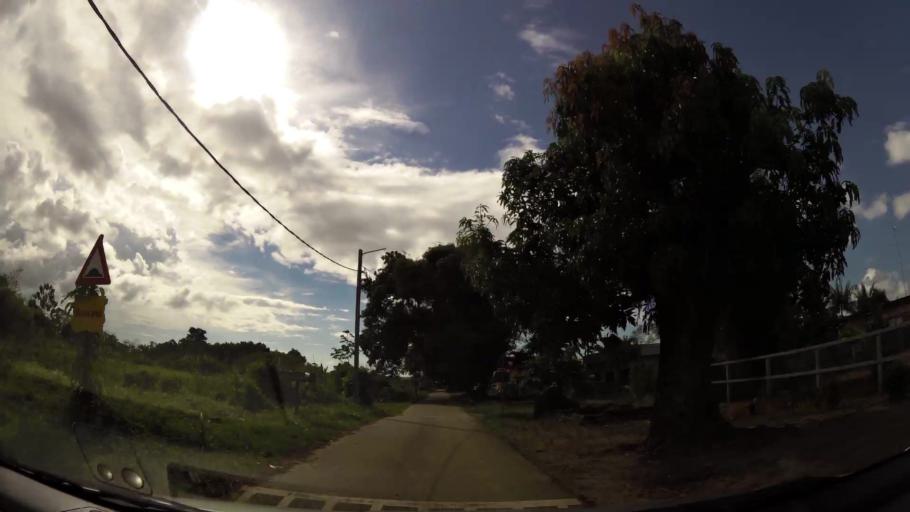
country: SR
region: Paramaribo
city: Paramaribo
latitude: 5.8510
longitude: -55.1596
